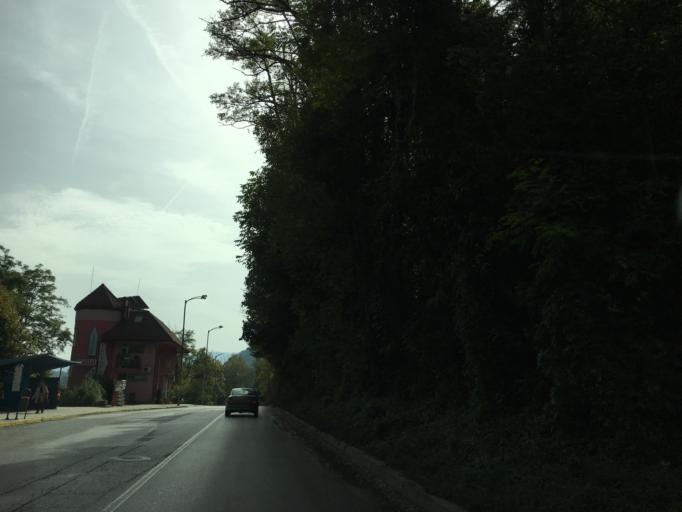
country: BG
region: Sofia-Capital
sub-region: Stolichna Obshtina
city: Sofia
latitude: 42.6029
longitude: 23.4026
